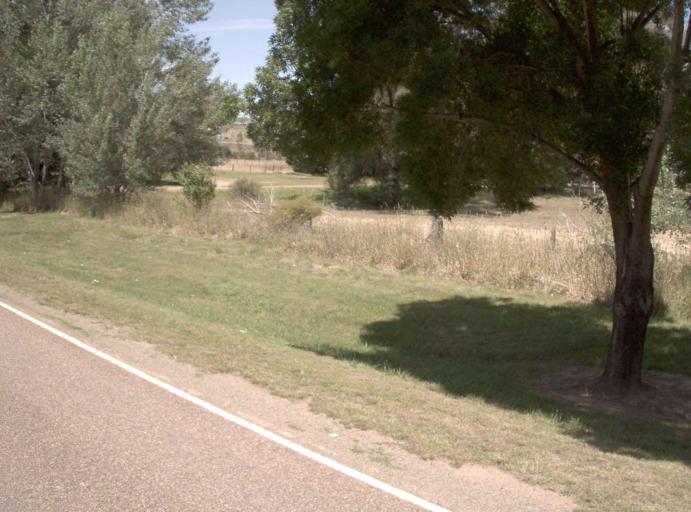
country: AU
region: Victoria
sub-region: East Gippsland
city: Bairnsdale
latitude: -37.2604
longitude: 147.7171
